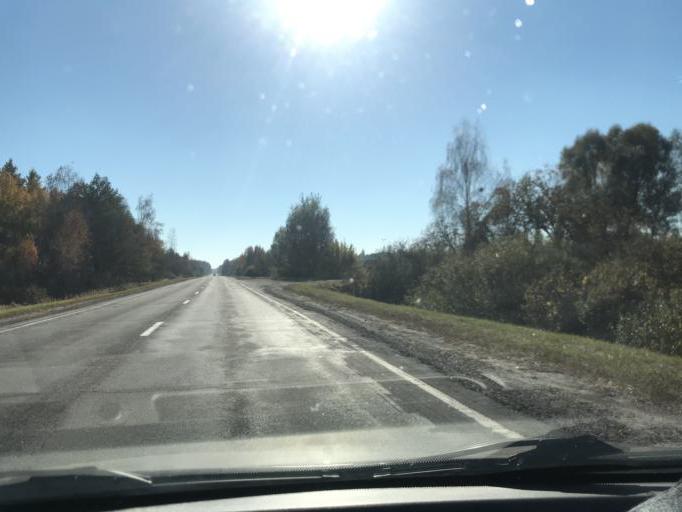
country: BY
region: Gomel
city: Kastsyukowka
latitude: 52.4429
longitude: 30.8252
